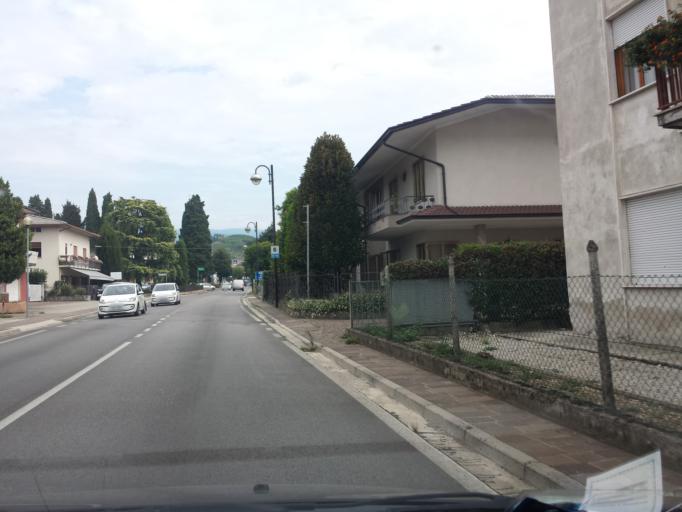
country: IT
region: Veneto
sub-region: Provincia di Vicenza
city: Breganze
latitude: 45.7034
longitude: 11.5648
